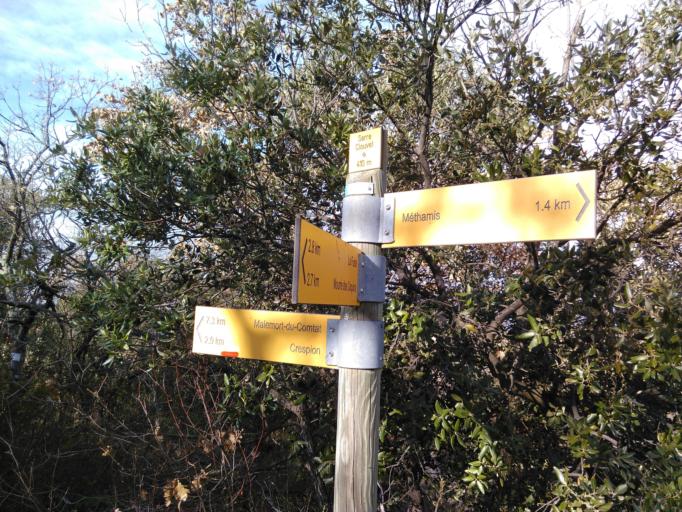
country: FR
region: Provence-Alpes-Cote d'Azur
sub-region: Departement du Vaucluse
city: Villes-sur-Auzon
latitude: 44.0036
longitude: 5.2190
